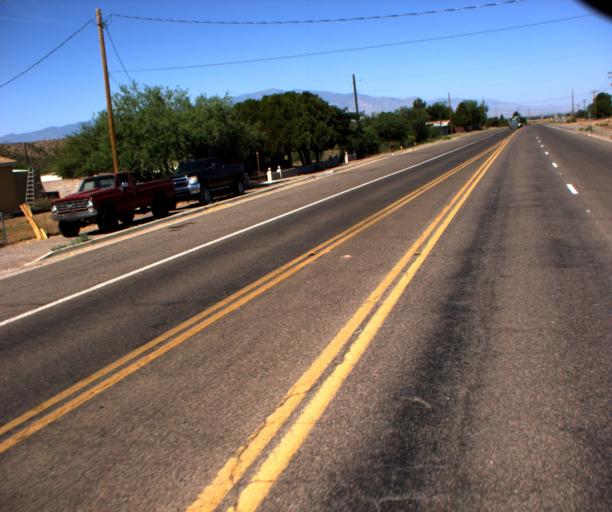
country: US
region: Arizona
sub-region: Graham County
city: Safford
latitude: 32.8129
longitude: -109.5983
